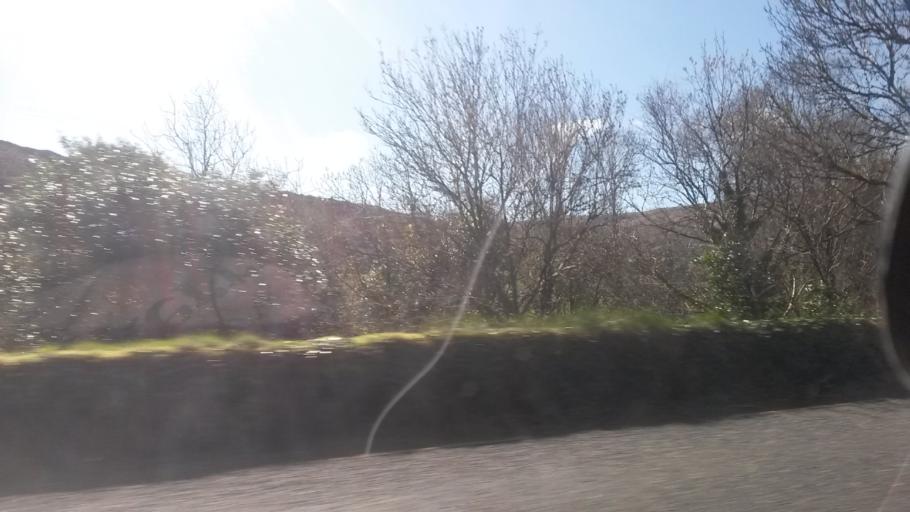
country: IE
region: Munster
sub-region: Ciarrai
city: Cill Airne
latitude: 51.9226
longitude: -9.3849
